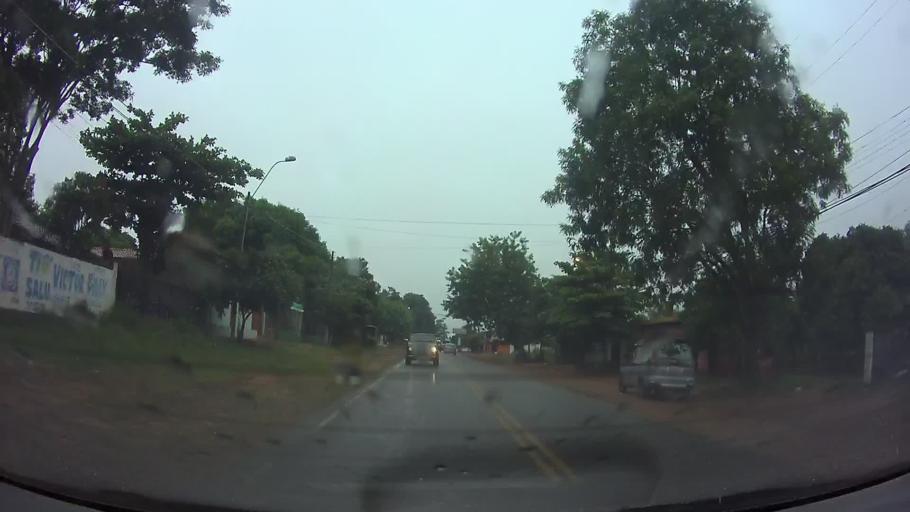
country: PY
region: Central
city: Ita
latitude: -25.5044
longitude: -57.3573
